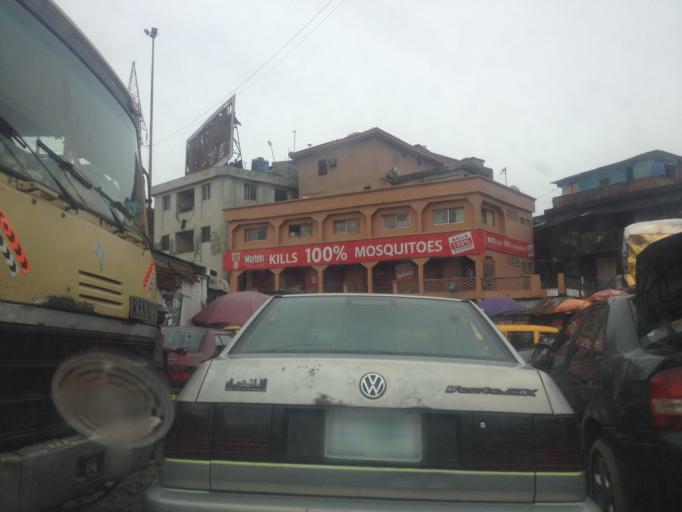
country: NG
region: Lagos
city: Lagos
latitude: 6.4616
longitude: 3.3830
